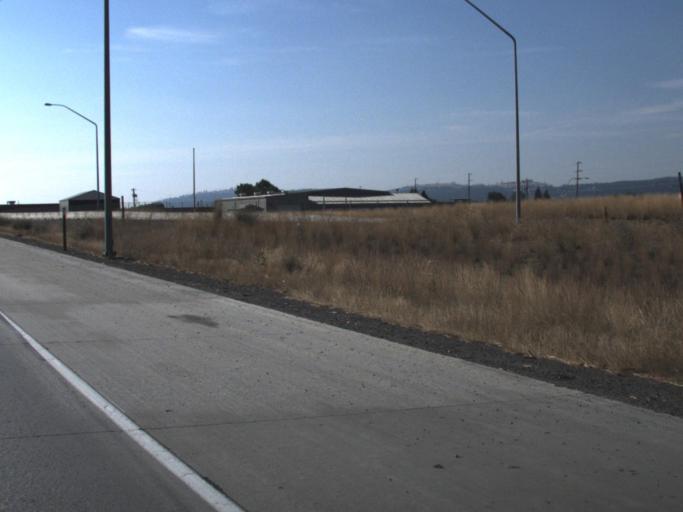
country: US
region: Washington
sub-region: Spokane County
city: Spokane Valley
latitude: 47.6741
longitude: -117.2424
